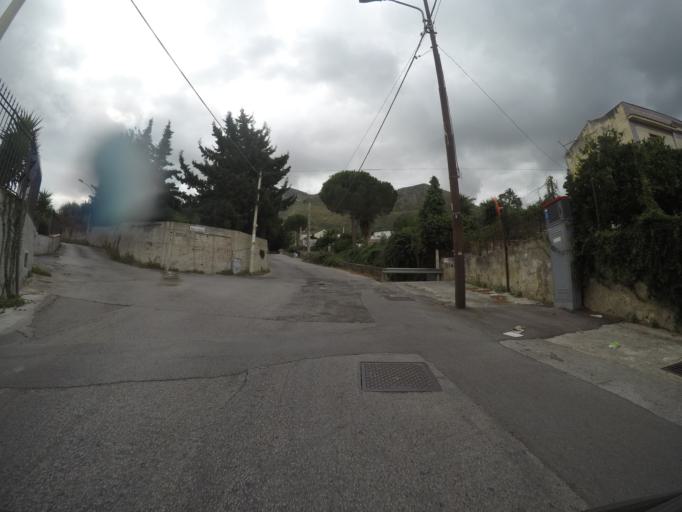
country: IT
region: Sicily
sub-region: Palermo
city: Carini
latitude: 38.1274
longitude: 13.1818
